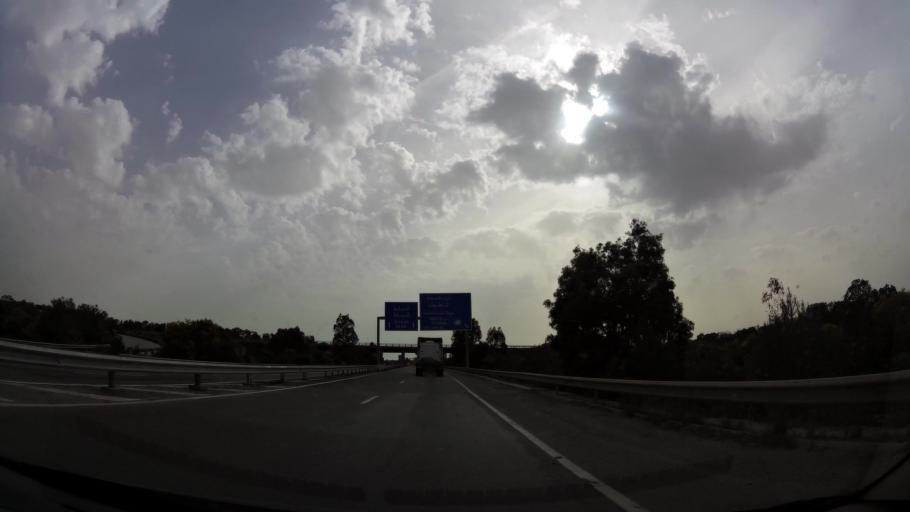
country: MA
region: Tanger-Tetouan
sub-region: Tanger-Assilah
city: Boukhalef
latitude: 35.6758
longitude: -5.9317
